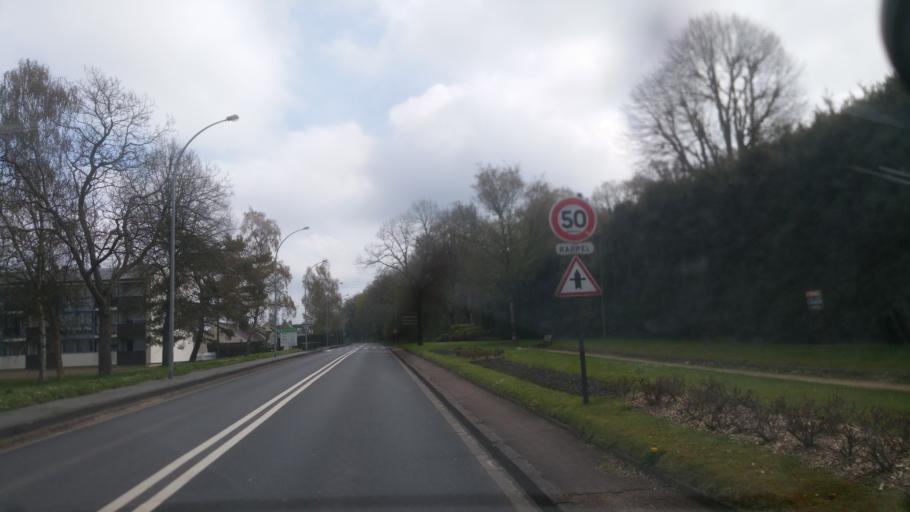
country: FR
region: Ile-de-France
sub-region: Departement de l'Essonne
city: Dourdan
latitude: 48.5233
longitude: 2.0066
